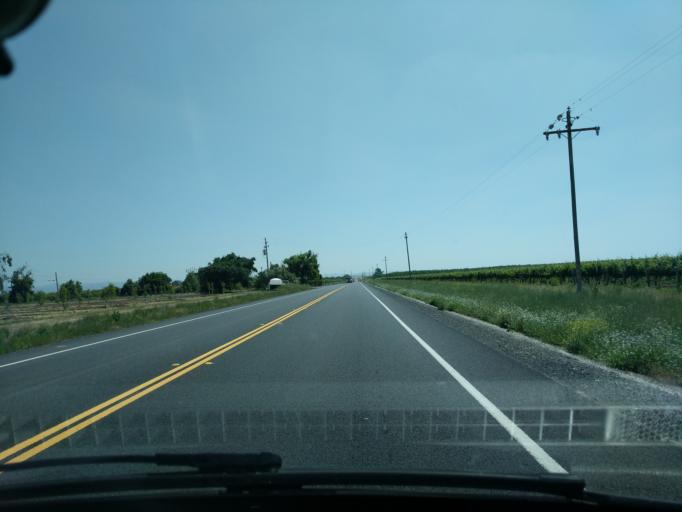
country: US
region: California
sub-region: San Joaquin County
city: Escalon
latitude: 37.9302
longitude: -120.9789
